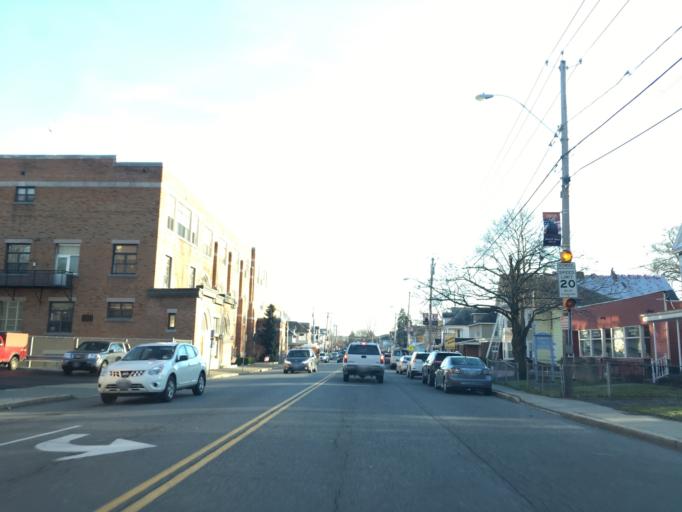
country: US
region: New York
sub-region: Rensselaer County
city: Wynantskill
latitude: 42.7089
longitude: -73.6632
